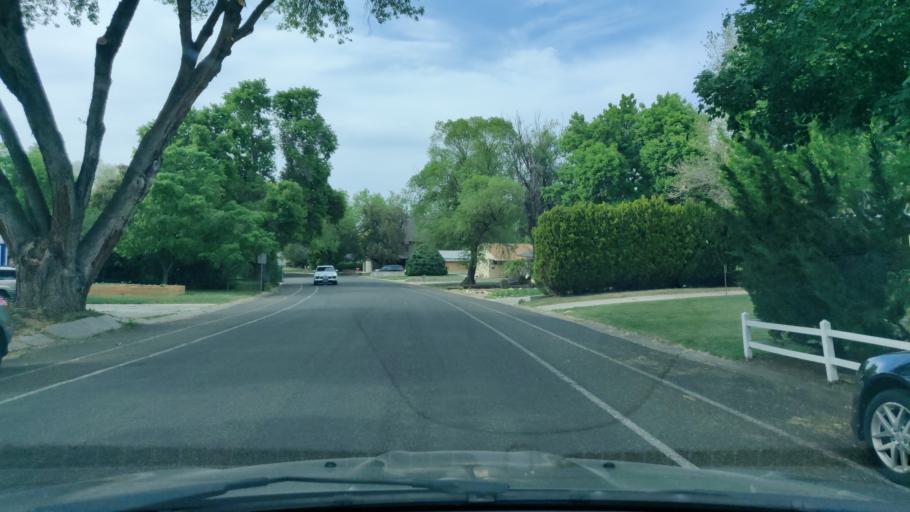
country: US
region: Utah
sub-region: Salt Lake County
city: Little Cottonwood Creek Valley
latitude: 40.6262
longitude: -111.8369
